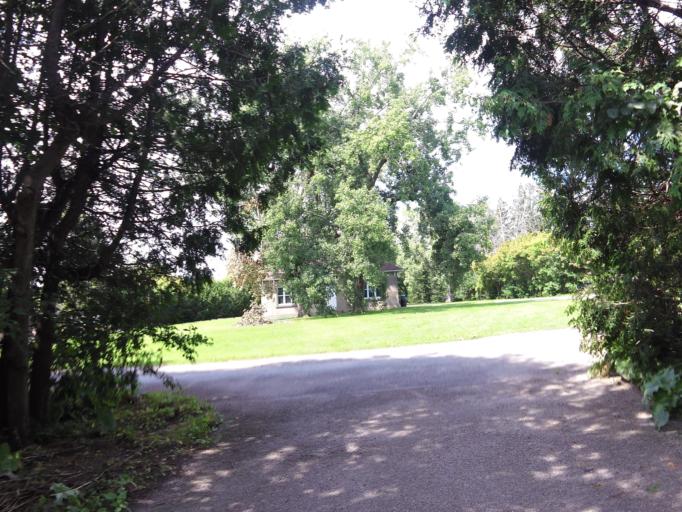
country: CA
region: Quebec
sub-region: Outaouais
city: Gatineau
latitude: 45.4551
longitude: -75.6762
